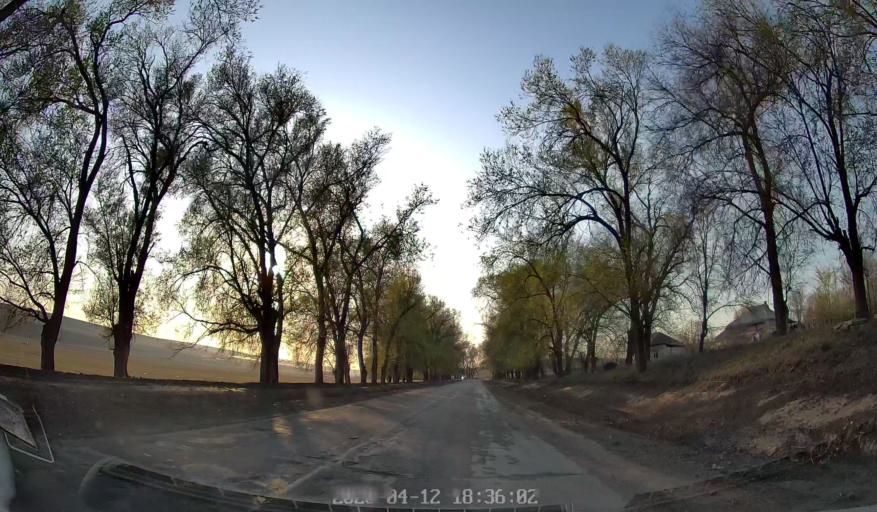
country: MD
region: Chisinau
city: Vadul lui Voda
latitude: 47.1156
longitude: 29.0369
